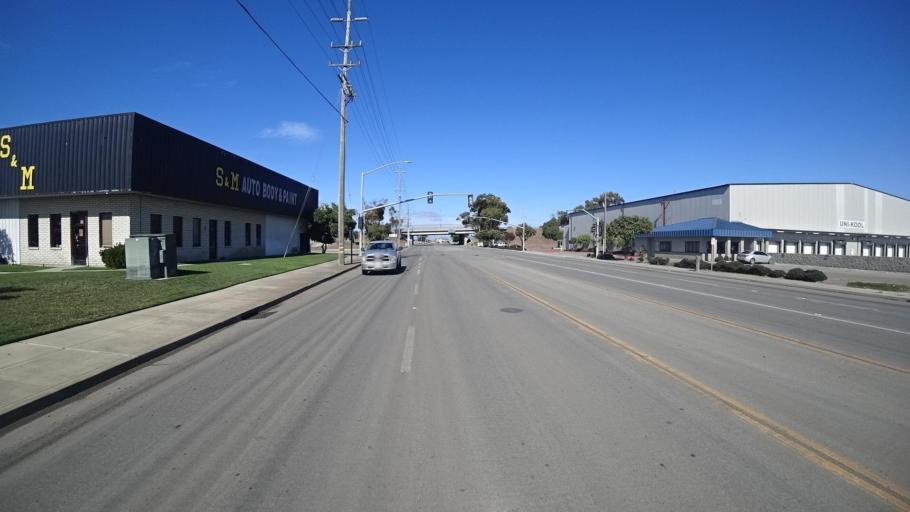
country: US
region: California
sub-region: Monterey County
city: Boronda
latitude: 36.6839
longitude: -121.6729
